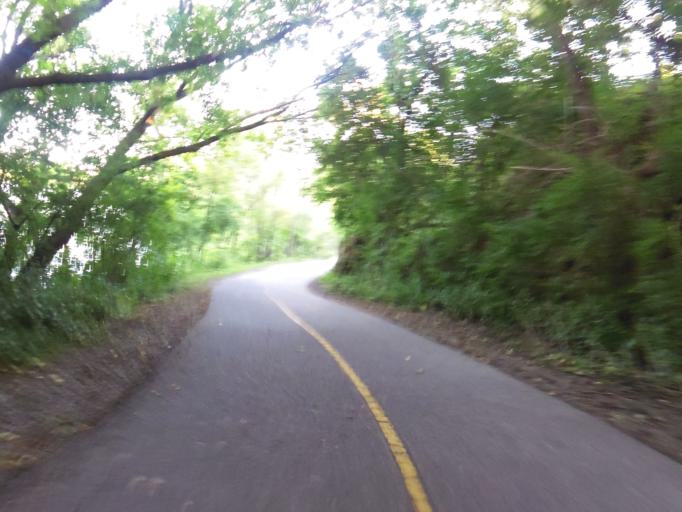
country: CA
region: Quebec
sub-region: Outaouais
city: Gatineau
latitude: 45.4504
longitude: -75.7274
